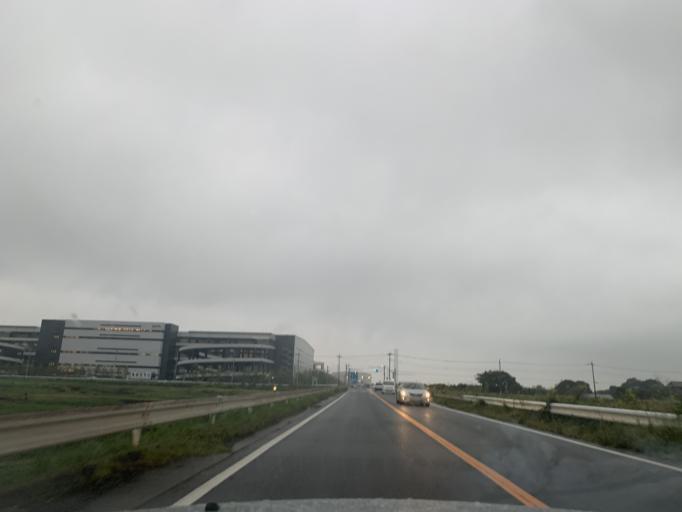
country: JP
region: Chiba
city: Nagareyama
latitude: 35.8901
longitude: 139.8951
